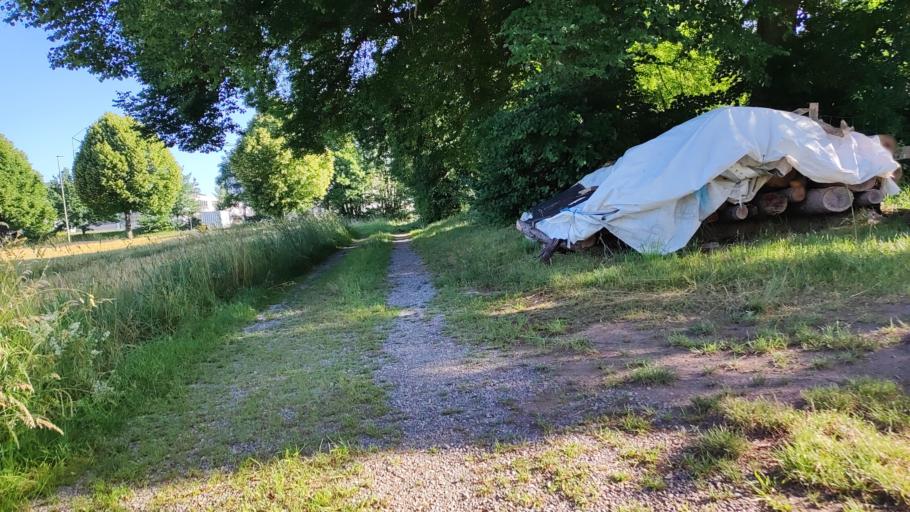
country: DE
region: Bavaria
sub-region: Swabia
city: Horgau
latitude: 48.3966
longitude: 10.6872
